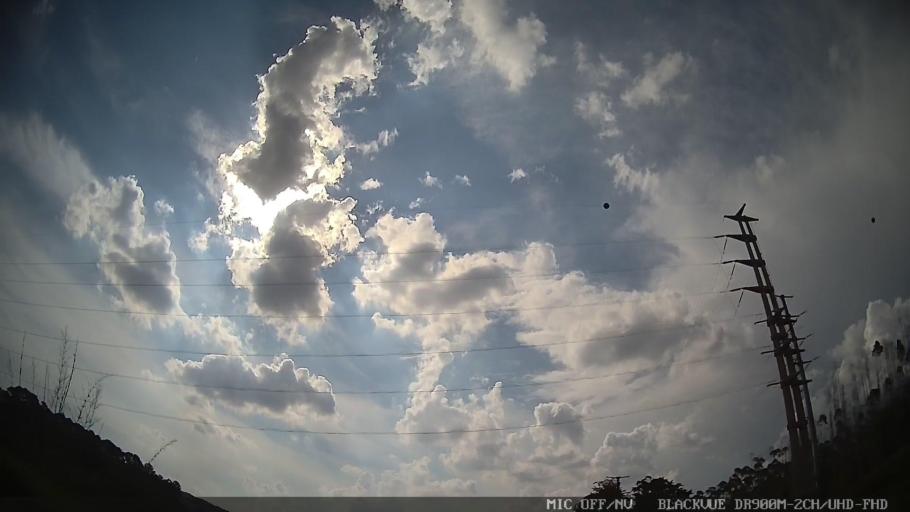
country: BR
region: Sao Paulo
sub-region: Braganca Paulista
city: Braganca Paulista
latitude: -22.9080
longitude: -46.5453
